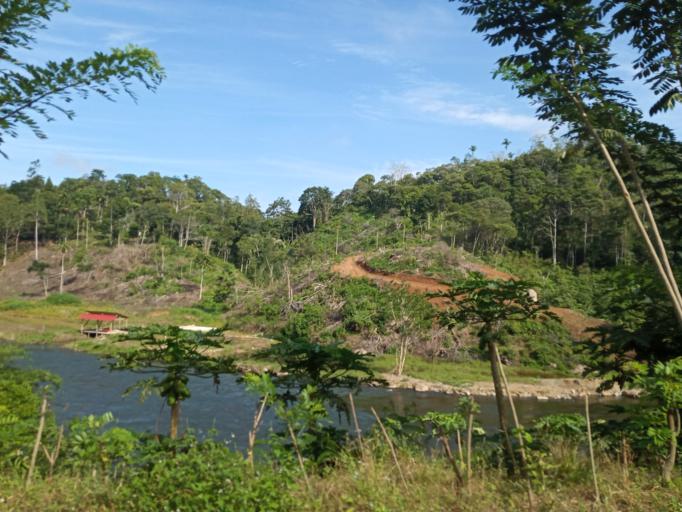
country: ID
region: Jambi
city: Sungai Penuh
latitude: -2.1491
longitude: 101.5672
